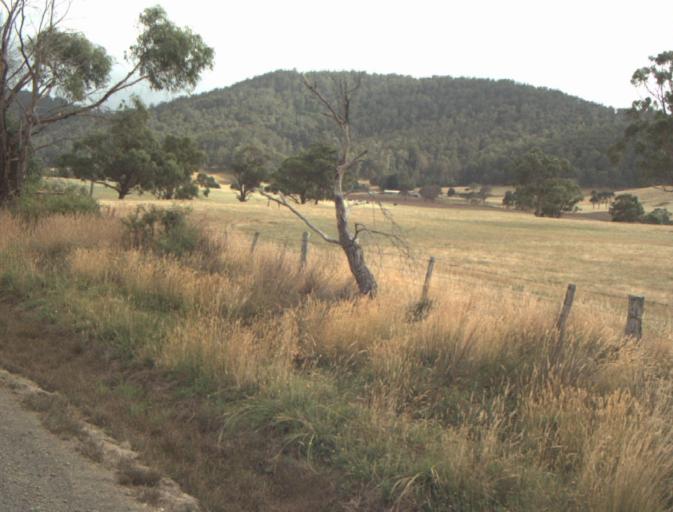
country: AU
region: Tasmania
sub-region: Dorset
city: Scottsdale
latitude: -41.4677
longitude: 147.5750
